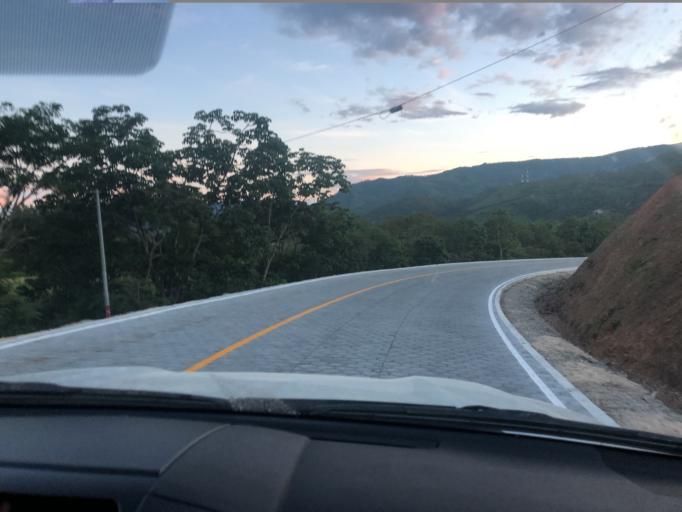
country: NI
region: Nueva Segovia
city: Ocotal
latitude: 13.6671
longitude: -86.6125
